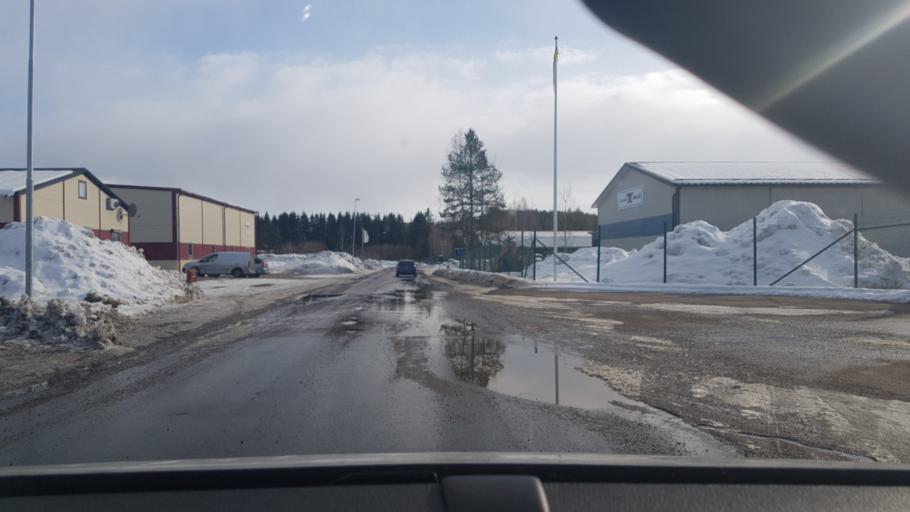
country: SE
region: Vaermland
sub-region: Arvika Kommun
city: Arvika
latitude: 59.6656
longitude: 12.6312
